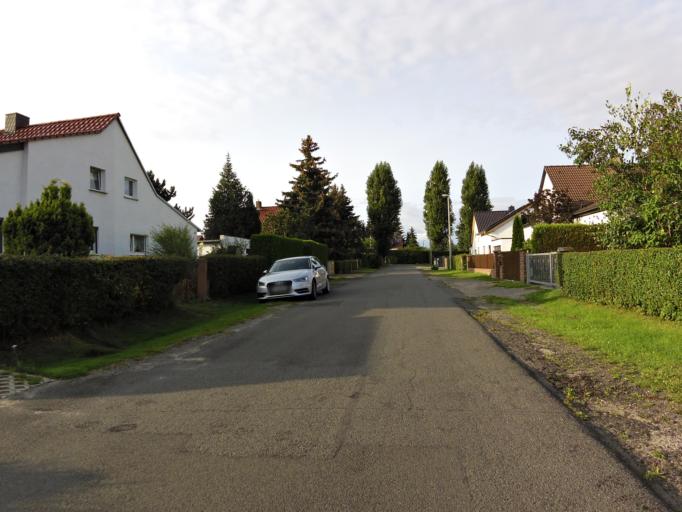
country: DE
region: Saxony
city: Leipzig
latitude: 51.3781
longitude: 12.4111
